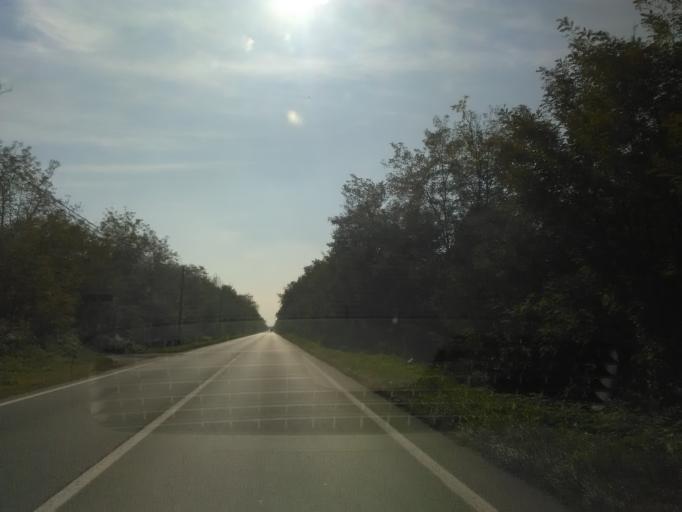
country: IT
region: Piedmont
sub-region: Provincia di Vercelli
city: Lenta
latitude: 45.5847
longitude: 8.3741
